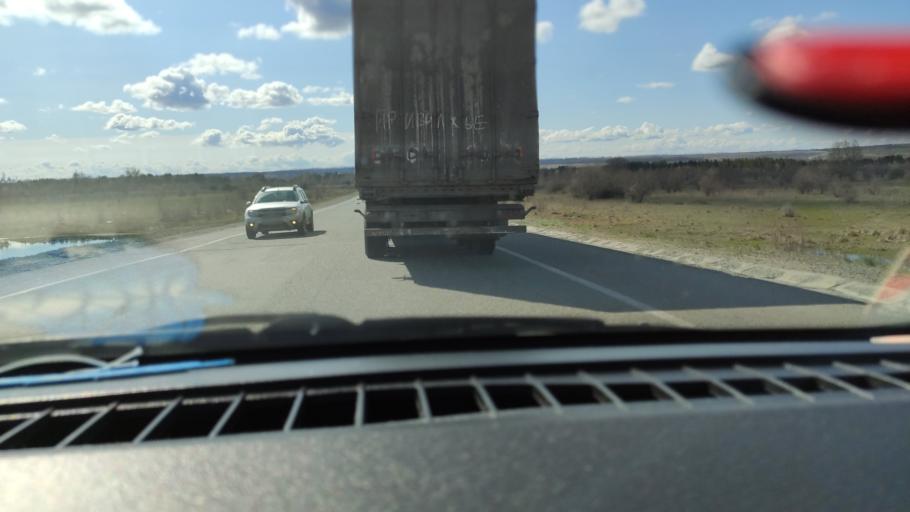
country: RU
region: Samara
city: Varlamovo
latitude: 53.1582
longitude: 48.2842
